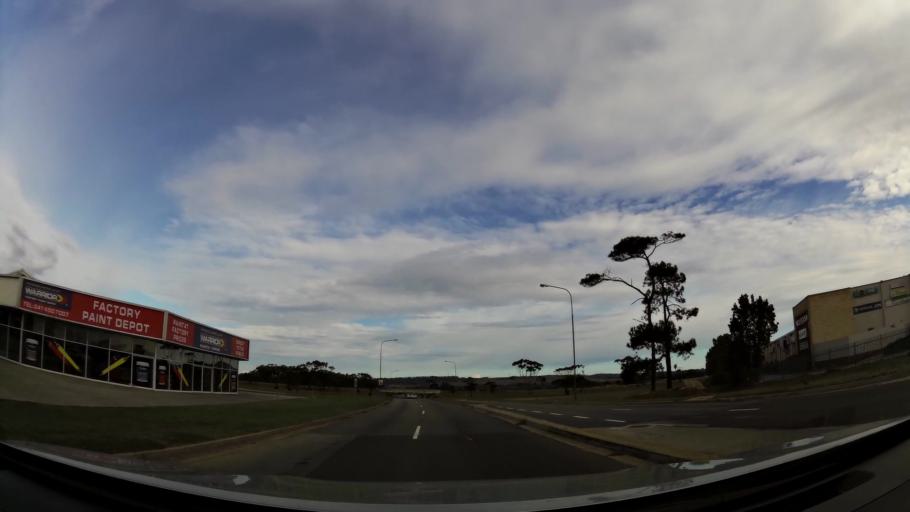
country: ZA
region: Eastern Cape
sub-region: Nelson Mandela Bay Metropolitan Municipality
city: Port Elizabeth
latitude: -33.9458
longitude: 25.5107
